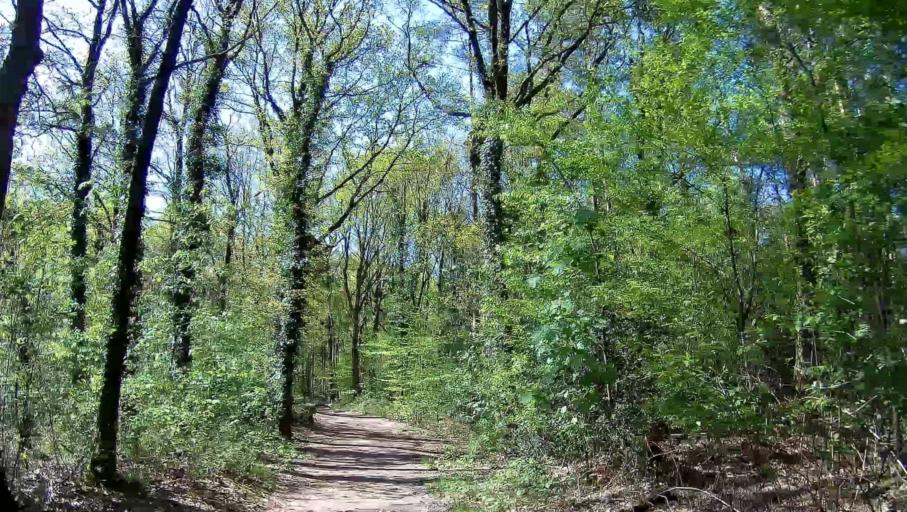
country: NL
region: Drenthe
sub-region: Gemeente Borger-Odoorn
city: Borger
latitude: 52.9582
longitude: 6.8000
